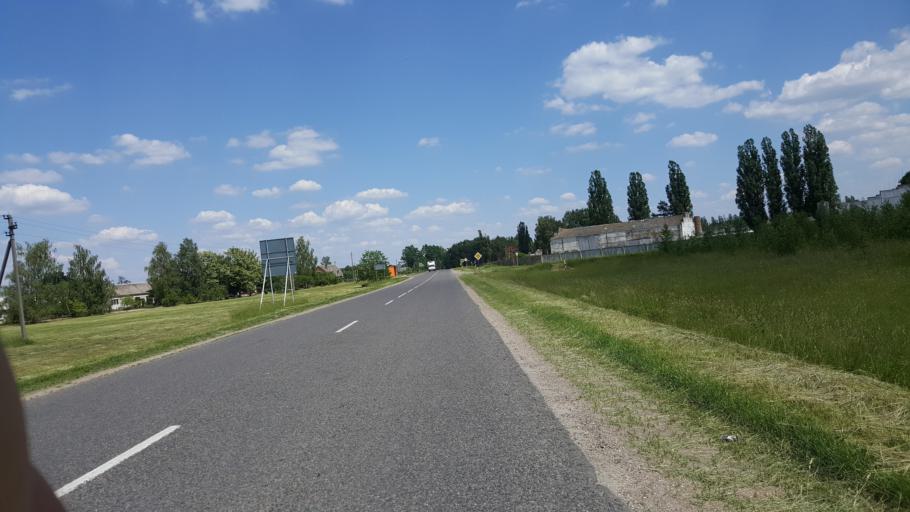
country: BY
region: Brest
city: Kobryn
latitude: 52.2284
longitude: 24.3014
